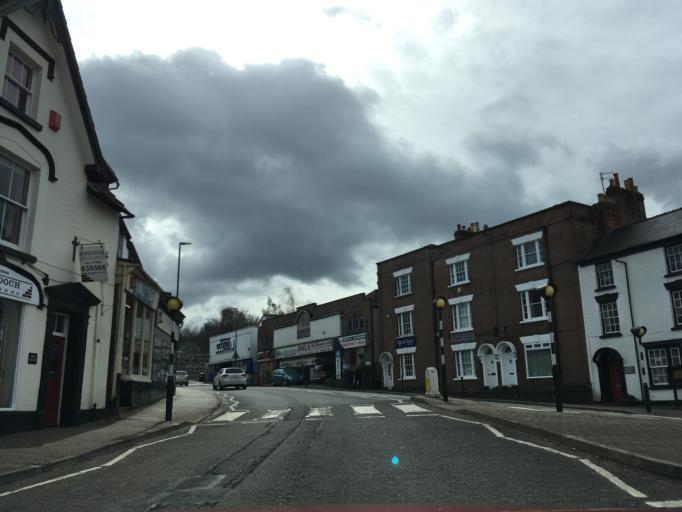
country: GB
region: England
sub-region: Gloucestershire
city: Coleford
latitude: 51.7932
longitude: -2.6173
